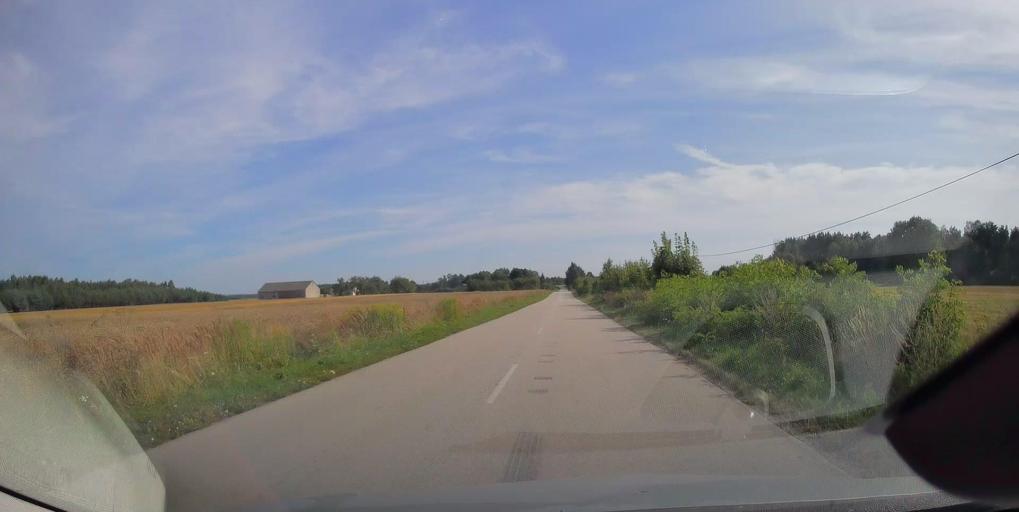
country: PL
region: Lodz Voivodeship
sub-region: Powiat opoczynski
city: Mniszkow
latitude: 51.3601
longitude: 20.0372
